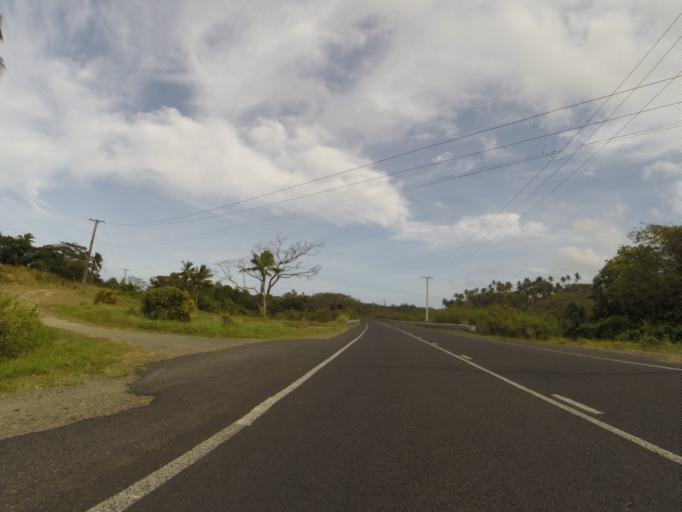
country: FJ
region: Western
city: Nadi
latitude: -18.1650
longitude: 177.4709
